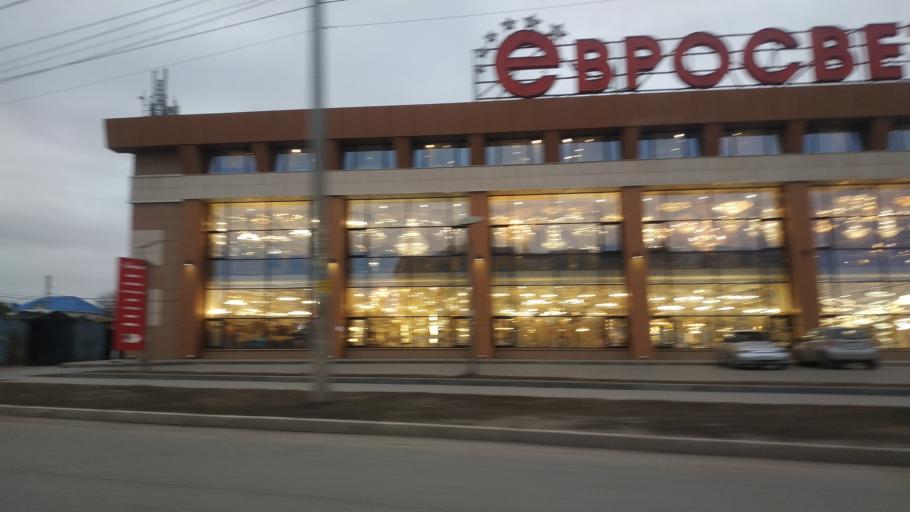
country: RU
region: Astrakhan
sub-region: Gorod Astrakhan'
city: Astrakhan'
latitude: 46.3326
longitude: 48.0123
